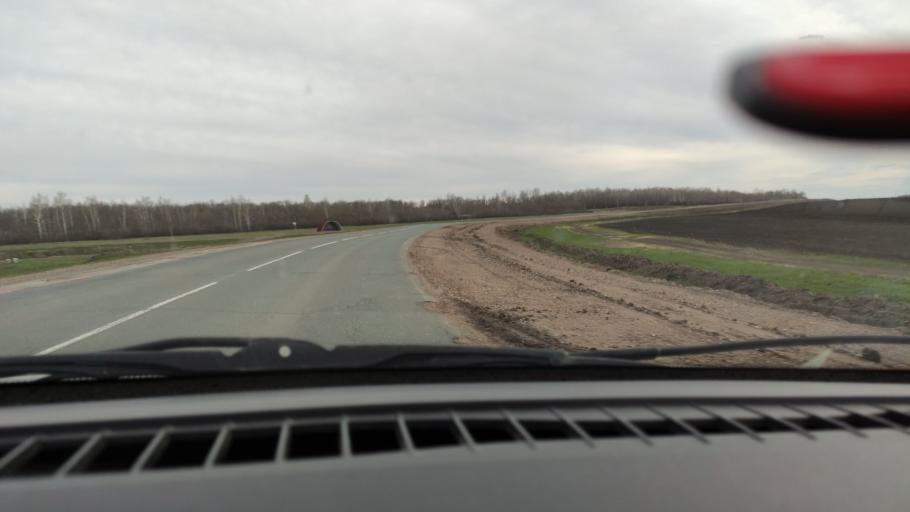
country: RU
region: Bashkortostan
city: Yermolayevo
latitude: 52.4652
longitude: 55.8305
